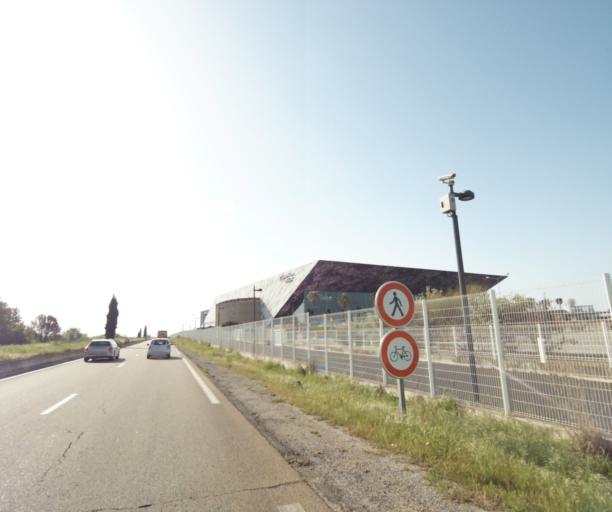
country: FR
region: Languedoc-Roussillon
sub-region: Departement de l'Herault
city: Perols
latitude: 43.5752
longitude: 3.9505
